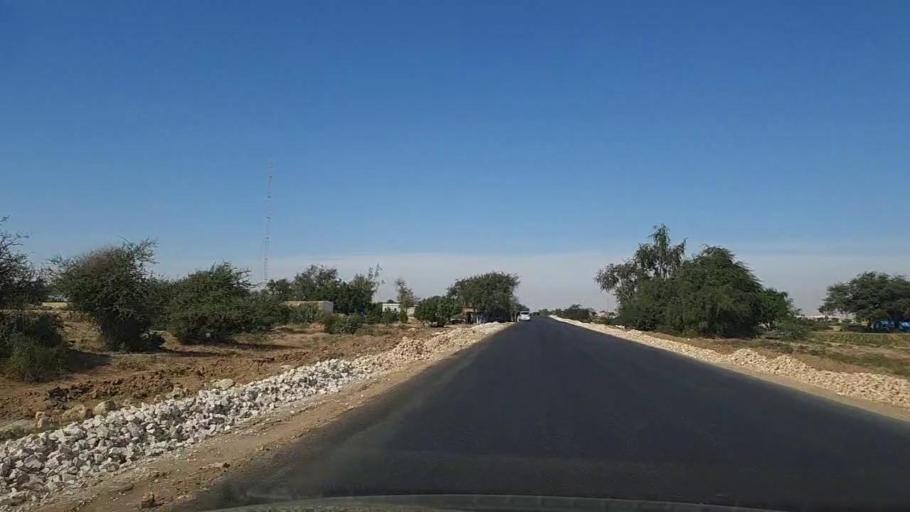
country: PK
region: Sindh
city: Kotri
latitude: 25.2836
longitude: 68.2104
